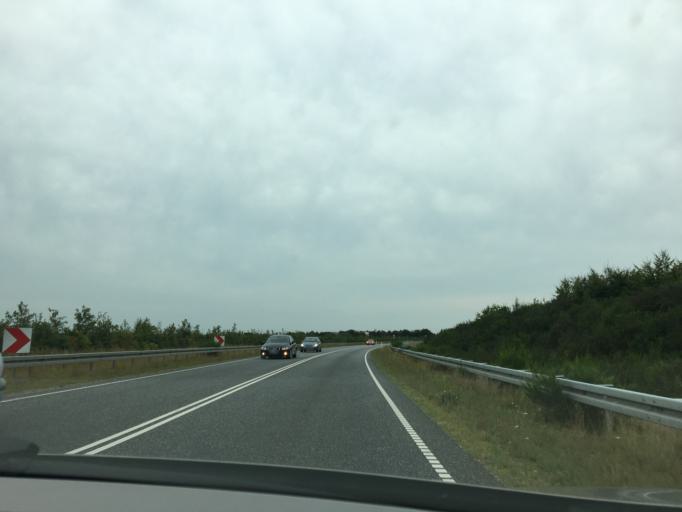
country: DK
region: Central Jutland
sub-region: Herning Kommune
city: Sunds
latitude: 56.2243
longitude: 9.0095
